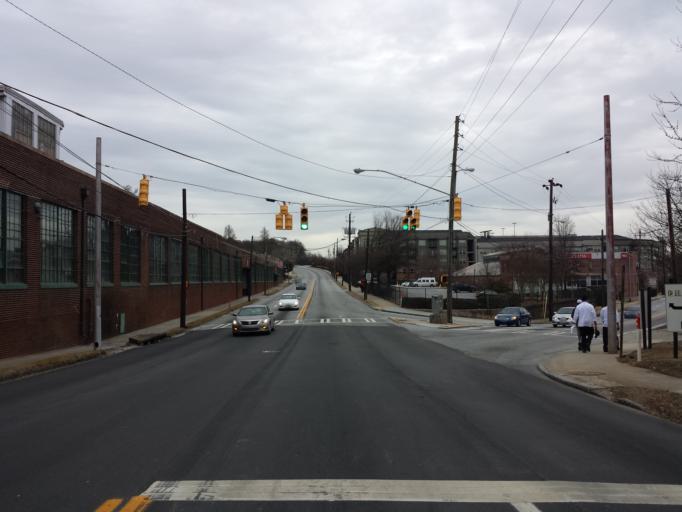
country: US
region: Georgia
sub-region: Fulton County
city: Atlanta
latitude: 33.7829
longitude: -84.4174
